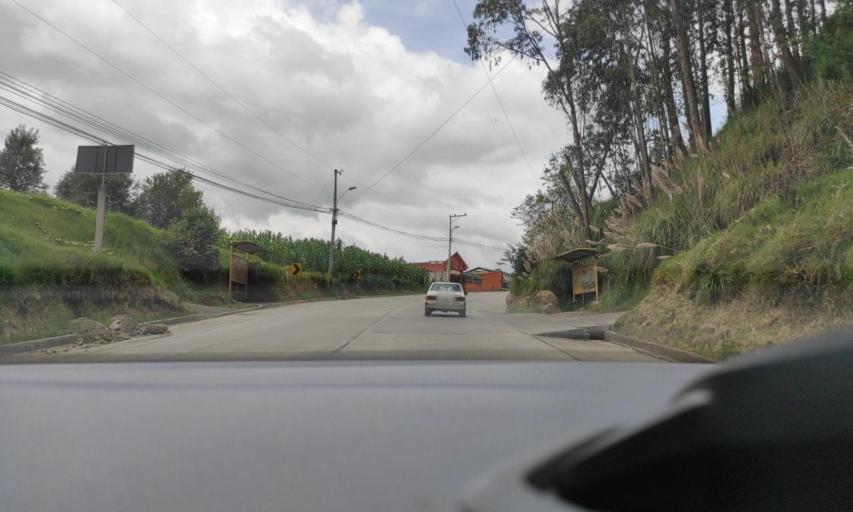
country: EC
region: Canar
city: Azogues
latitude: -2.7038
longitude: -78.8894
